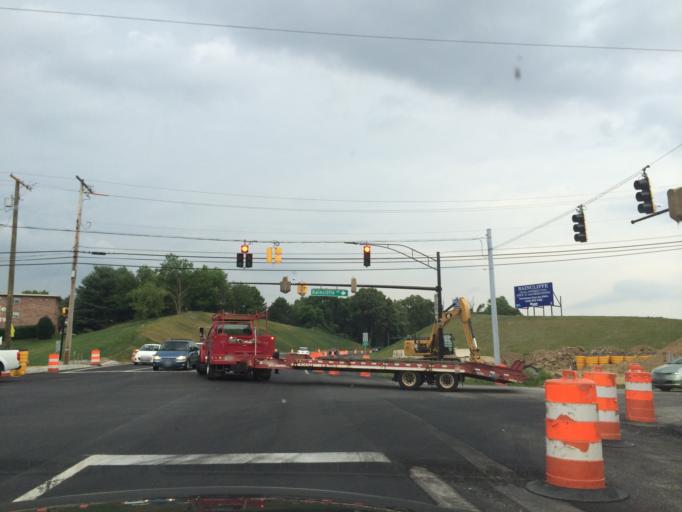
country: US
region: Maryland
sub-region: Carroll County
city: Sykesville
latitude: 39.3684
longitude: -76.9641
